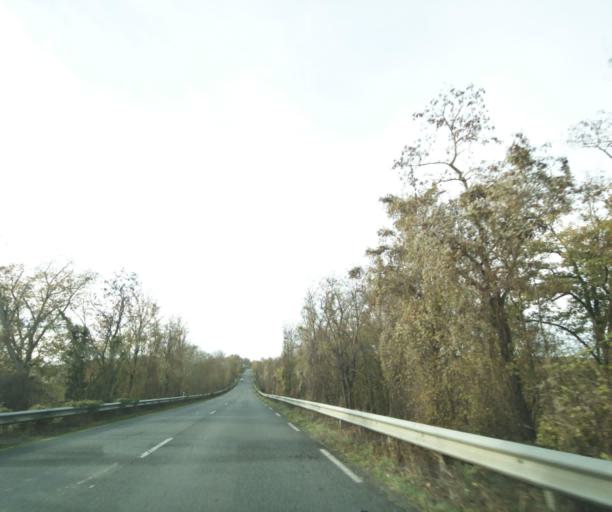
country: FR
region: Midi-Pyrenees
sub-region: Departement du Gers
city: Gimont
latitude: 43.6174
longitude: 0.9250
